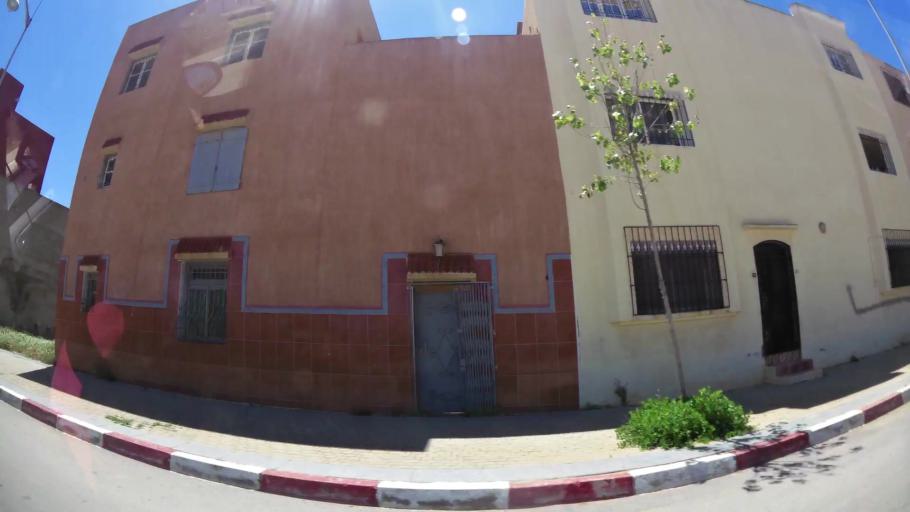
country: MA
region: Oriental
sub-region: Berkane-Taourirt
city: Madagh
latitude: 35.0844
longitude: -2.2288
